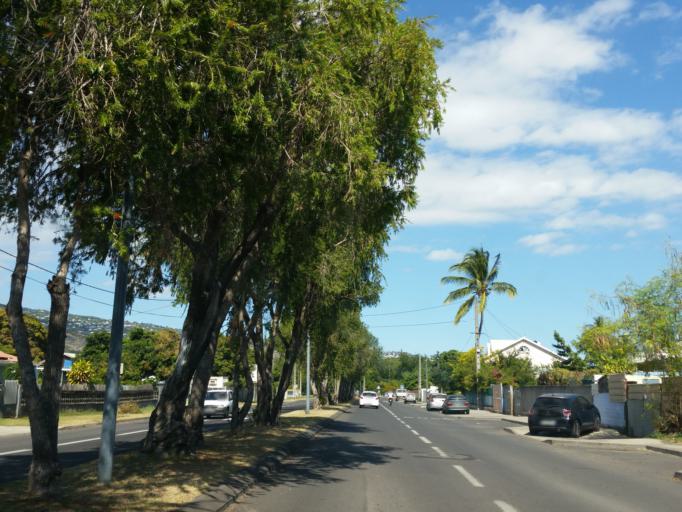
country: RE
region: Reunion
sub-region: Reunion
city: Saint-Paul
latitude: -20.9851
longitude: 55.2889
